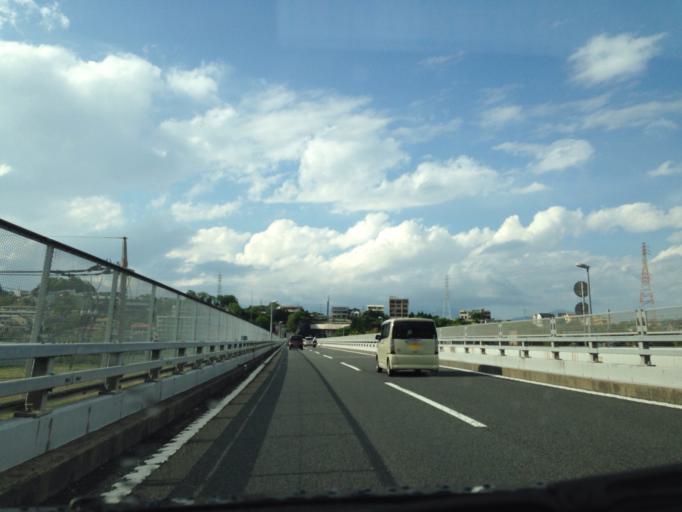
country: JP
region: Kanagawa
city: Odawara
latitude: 35.2704
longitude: 139.1504
